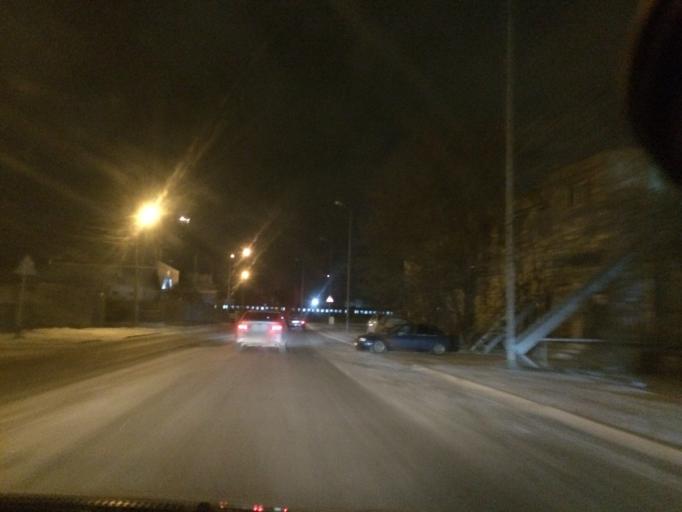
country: KZ
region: Astana Qalasy
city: Astana
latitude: 51.2009
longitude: 71.3870
